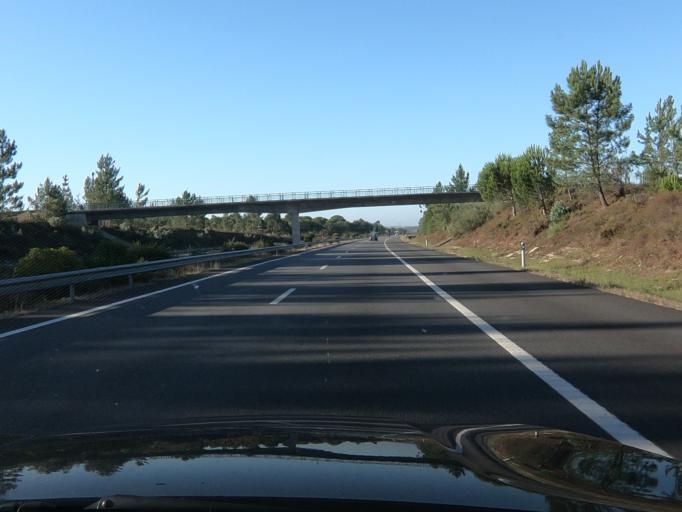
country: PT
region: Setubal
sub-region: Alcacer do Sal
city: Alcacer do Sal
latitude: 38.4624
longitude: -8.5282
